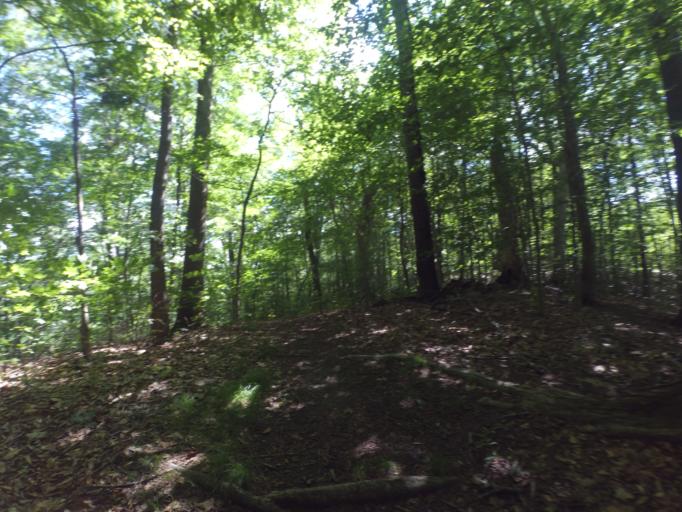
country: US
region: Ohio
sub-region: Portage County
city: Streetsboro
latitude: 41.2118
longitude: -81.3638
